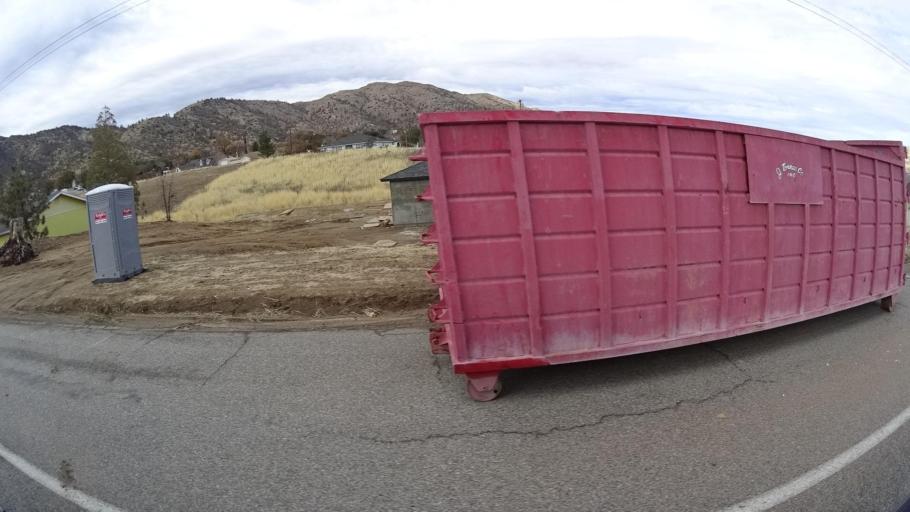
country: US
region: California
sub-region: Kern County
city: Golden Hills
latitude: 35.1425
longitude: -118.5043
